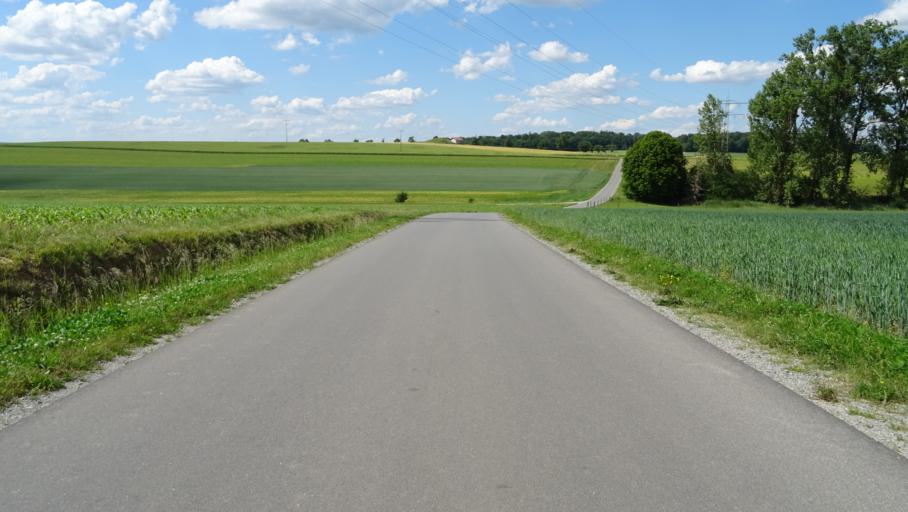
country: DE
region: Baden-Wuerttemberg
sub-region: Karlsruhe Region
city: Adelsheim
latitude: 49.3993
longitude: 9.3674
